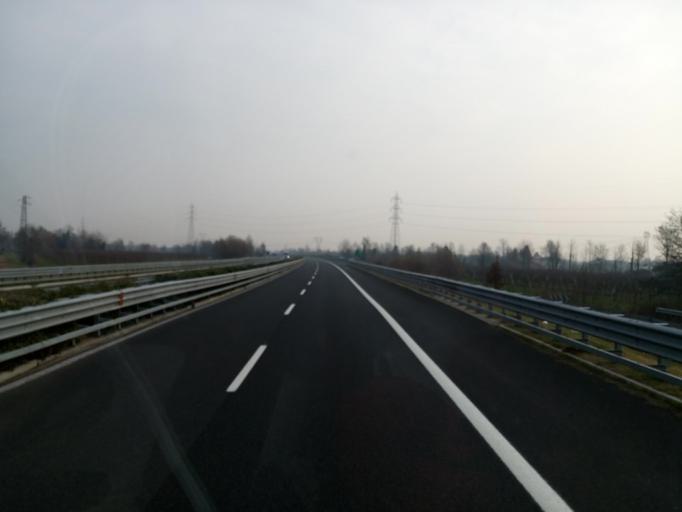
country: IT
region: Veneto
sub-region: Provincia di Treviso
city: Bibano
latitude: 45.8909
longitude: 12.4214
